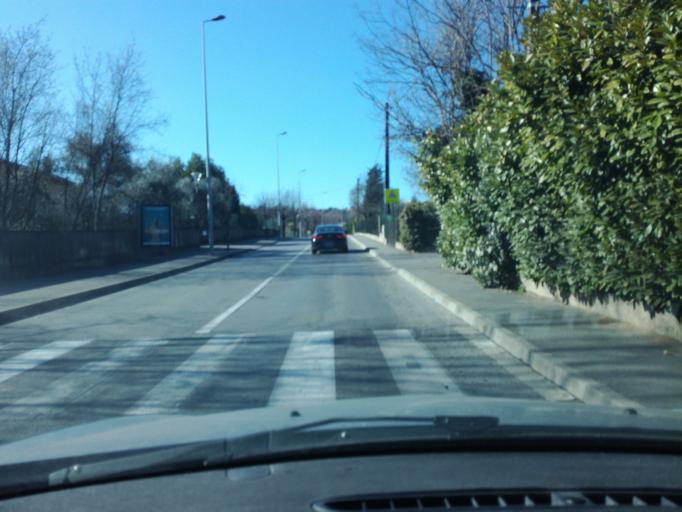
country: FR
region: Provence-Alpes-Cote d'Azur
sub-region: Departement des Alpes-Maritimes
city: Mouans-Sartoux
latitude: 43.6443
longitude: 6.9540
